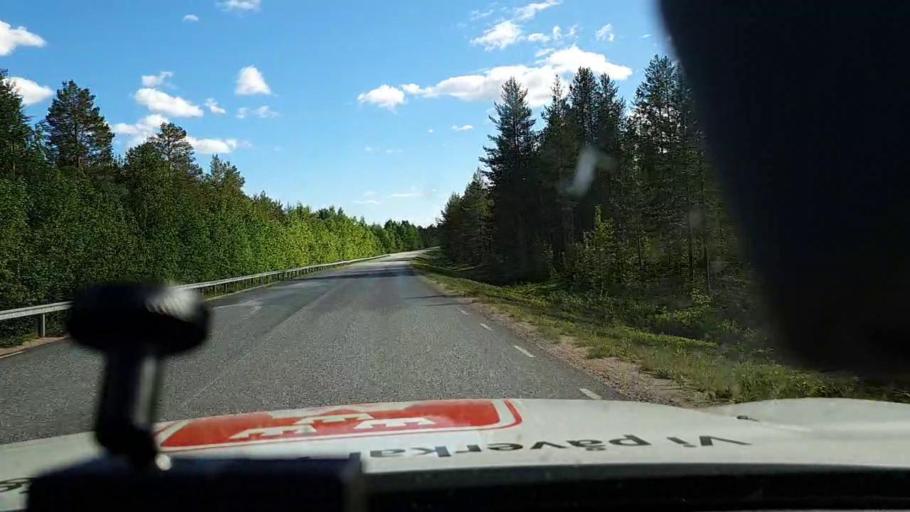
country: SE
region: Norrbotten
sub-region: Overtornea Kommun
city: OEvertornea
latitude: 66.3452
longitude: 23.6483
